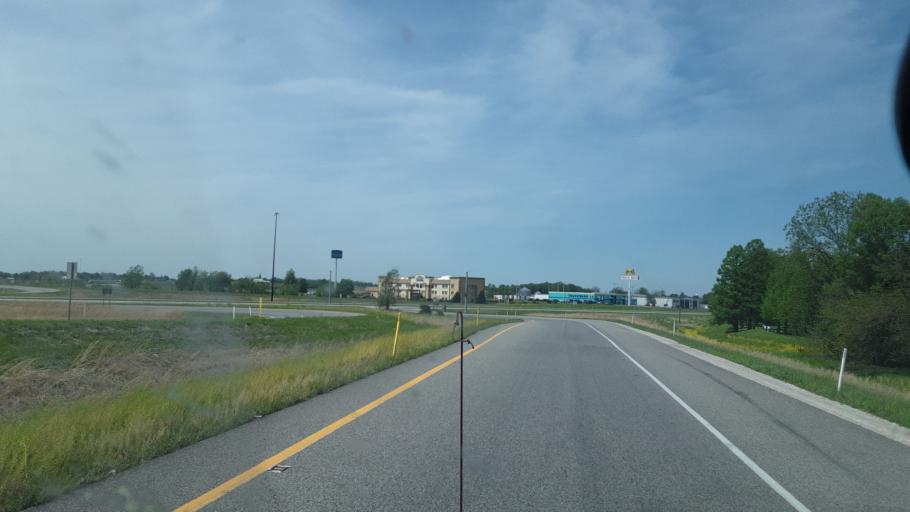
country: US
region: Indiana
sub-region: Gibson County
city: Haubstadt
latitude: 38.1681
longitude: -87.5483
